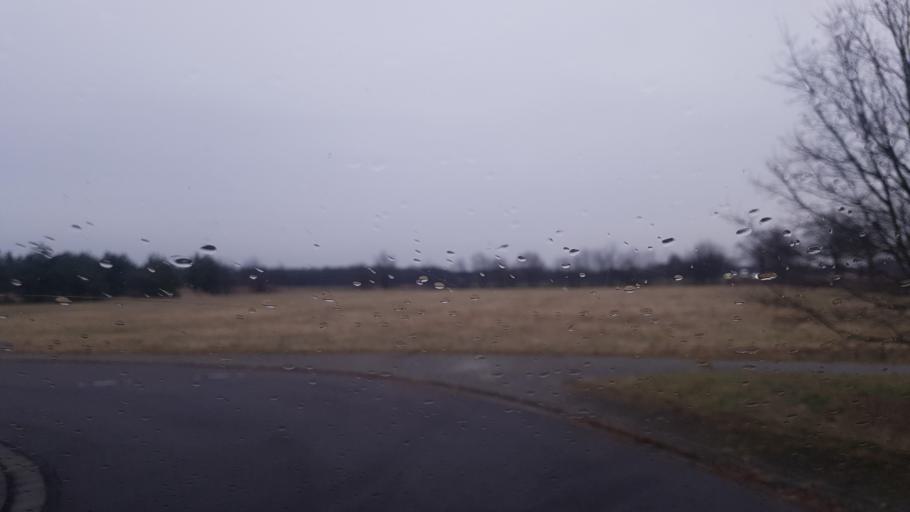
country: DE
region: Brandenburg
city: Schwarzheide
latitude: 51.4710
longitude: 13.8285
